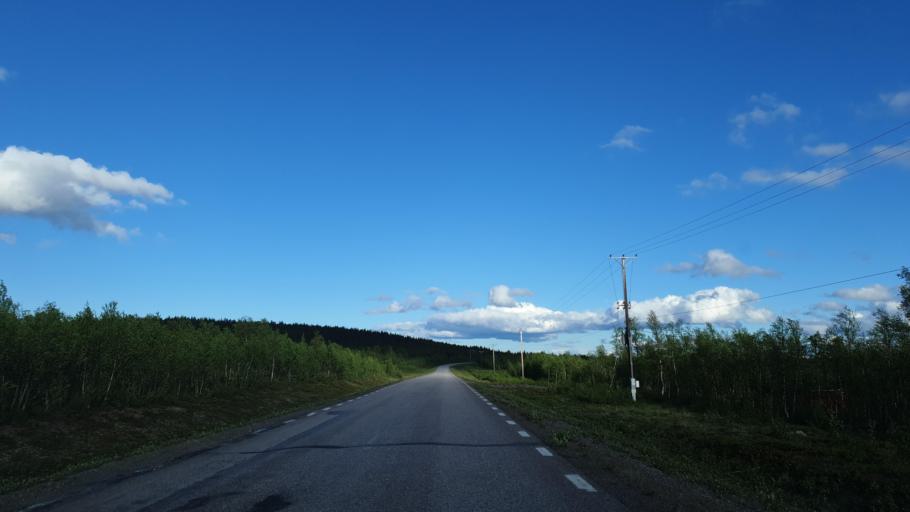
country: SE
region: Norrbotten
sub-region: Kiruna Kommun
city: Kiruna
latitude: 67.7603
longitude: 20.0100
